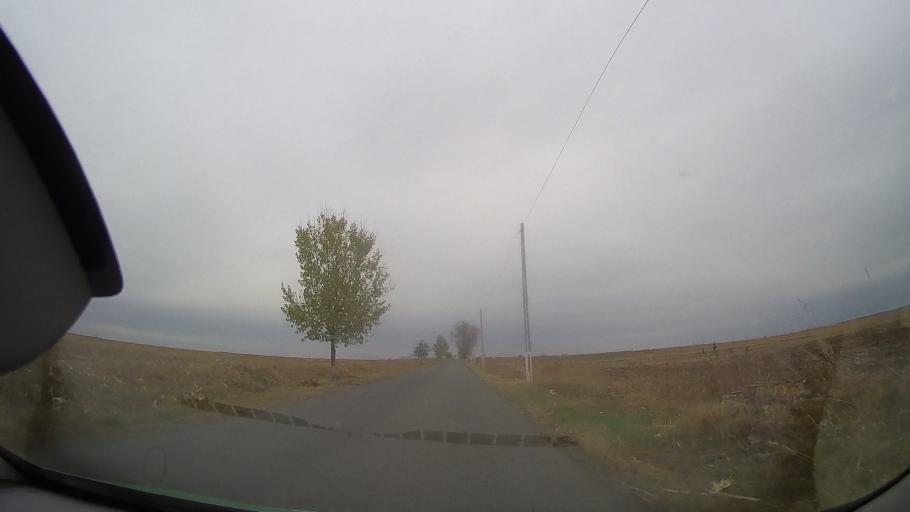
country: RO
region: Braila
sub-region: Comuna Budesti
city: Tataru
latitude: 44.8629
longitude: 27.4256
